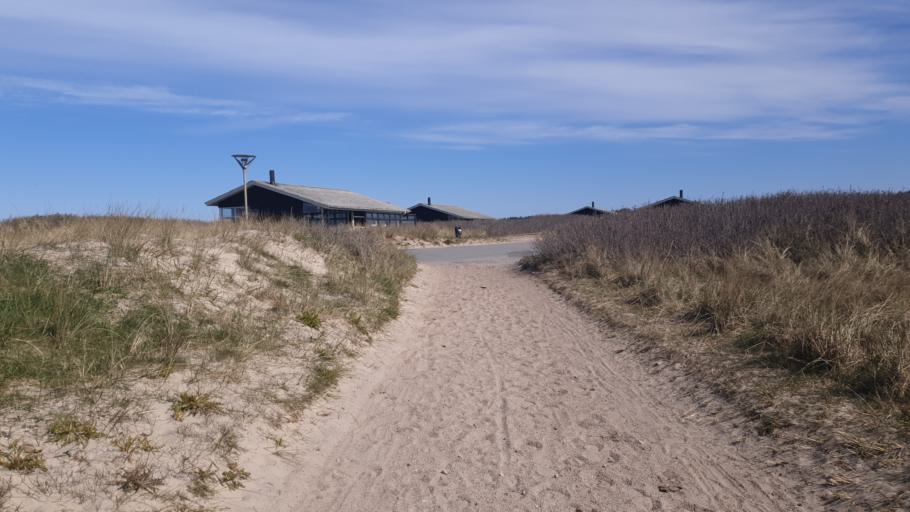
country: DK
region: North Denmark
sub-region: Hjorring Kommune
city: Hjorring
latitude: 57.4949
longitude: 9.8316
